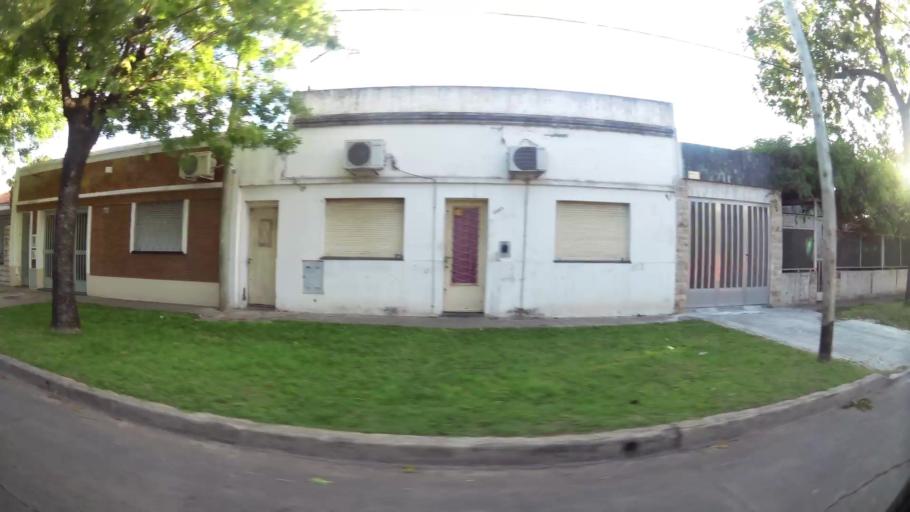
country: AR
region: Santa Fe
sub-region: Departamento de Rosario
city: Rosario
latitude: -32.9741
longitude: -60.6678
